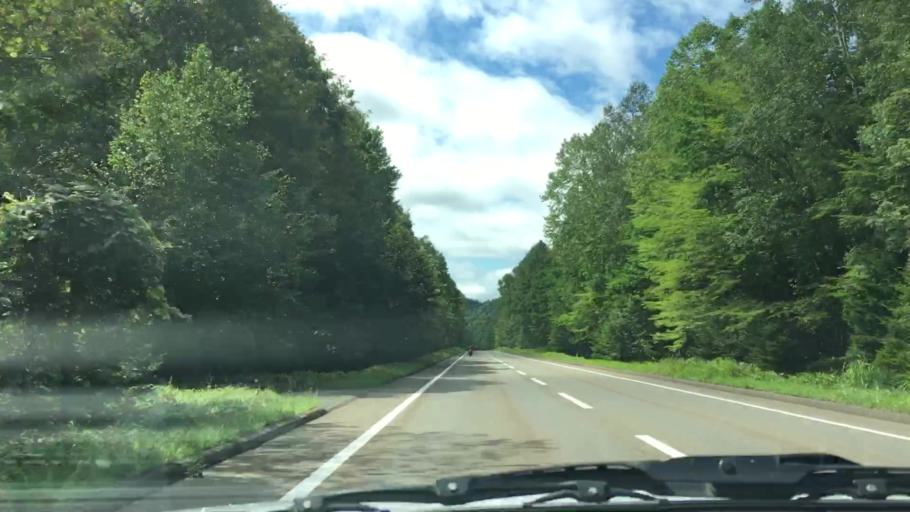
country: JP
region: Hokkaido
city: Kitami
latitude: 43.4027
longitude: 143.9318
